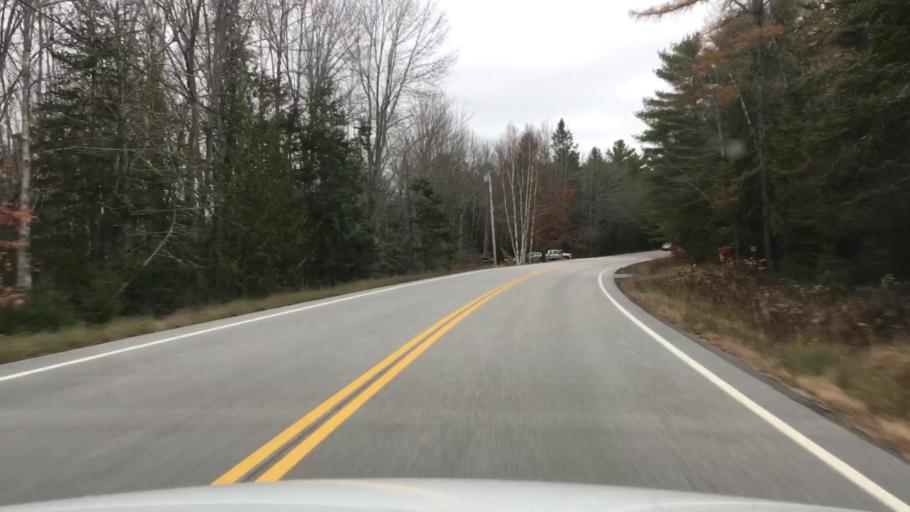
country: US
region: Maine
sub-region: Hancock County
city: Penobscot
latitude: 44.5041
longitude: -68.6550
